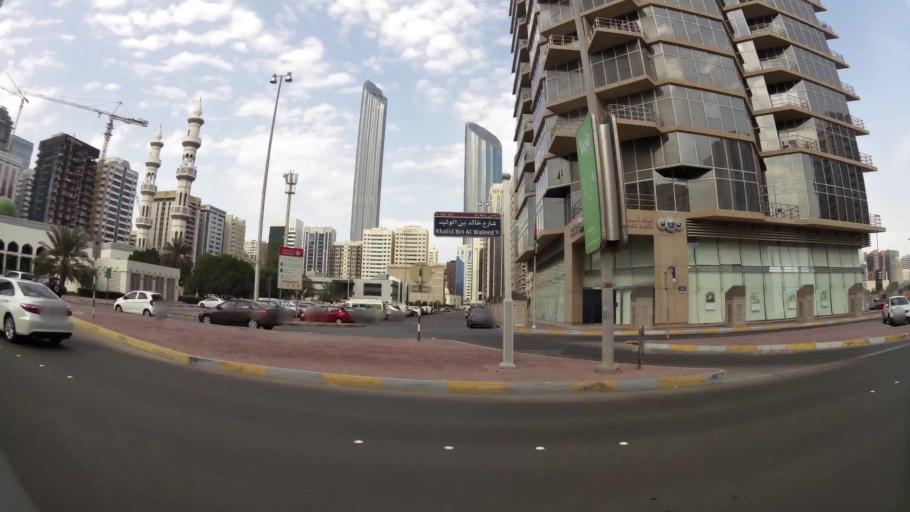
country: AE
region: Abu Dhabi
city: Abu Dhabi
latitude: 24.4831
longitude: 54.3531
